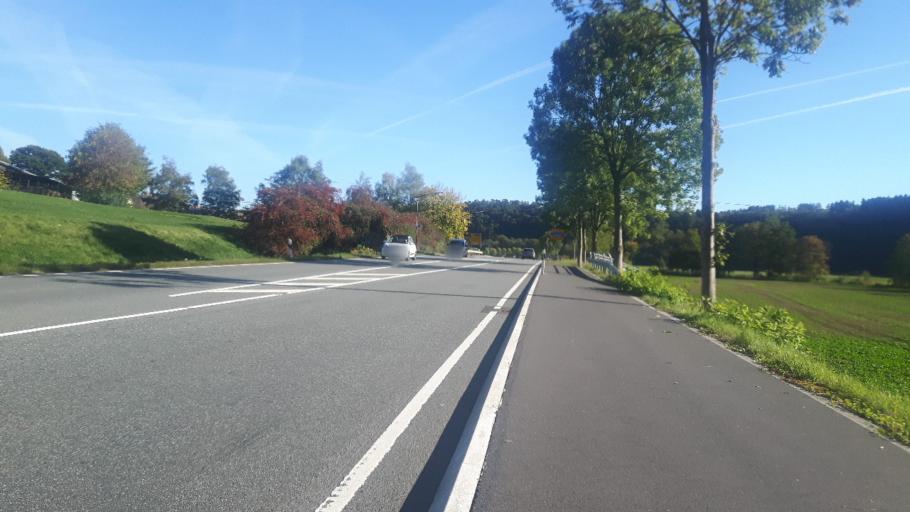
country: DE
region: Rheinland-Pfalz
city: Katzwinkel
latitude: 50.8028
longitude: 7.7999
